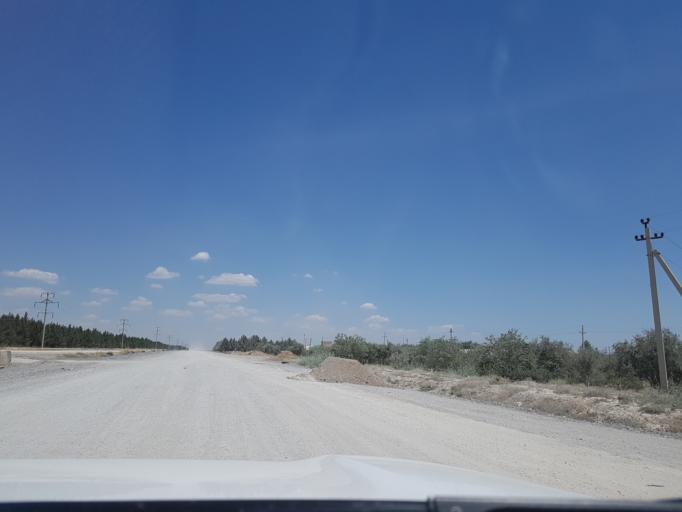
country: TM
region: Ahal
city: Abadan
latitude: 38.1738
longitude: 57.9495
